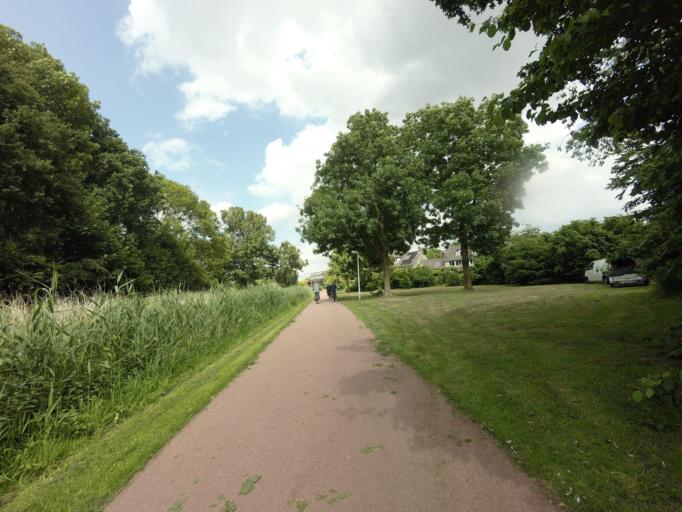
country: NL
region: North Holland
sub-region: Gemeente Huizen
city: Huizen
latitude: 52.2912
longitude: 5.2598
